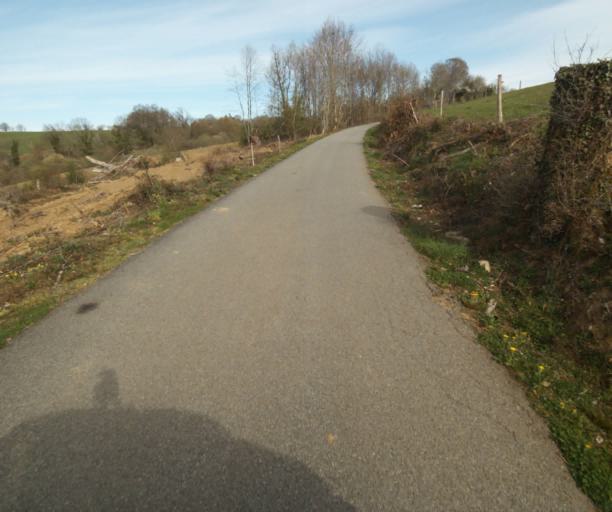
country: FR
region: Limousin
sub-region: Departement de la Correze
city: Chamboulive
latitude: 45.4183
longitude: 1.7895
